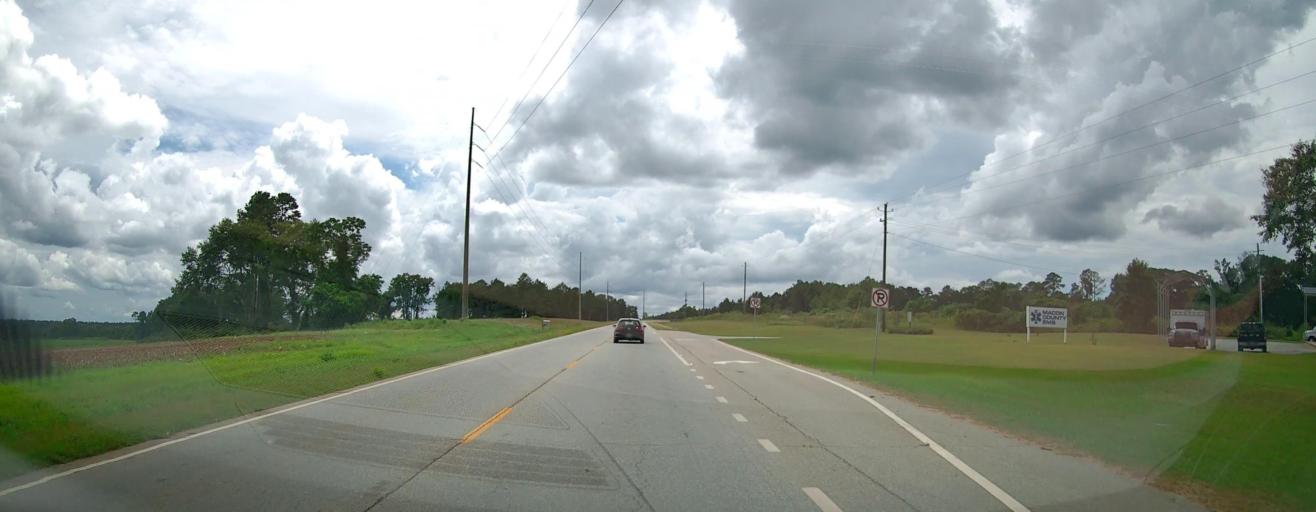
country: US
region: Georgia
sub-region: Macon County
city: Oglethorpe
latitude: 32.2783
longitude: -84.0651
